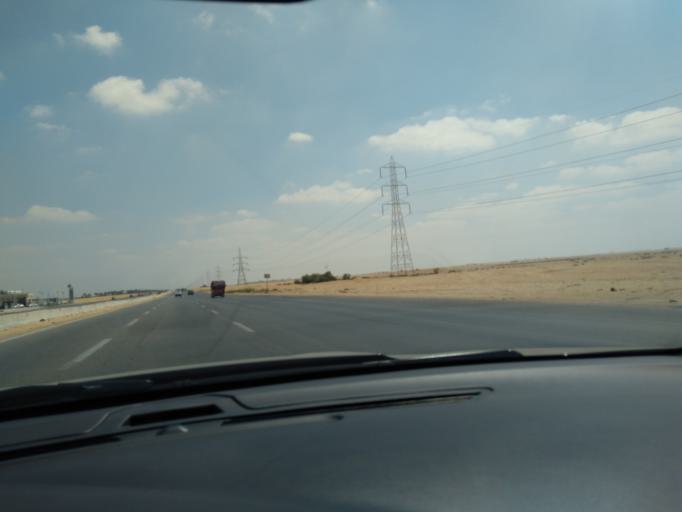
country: EG
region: Al Isma'iliyah
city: At Tall al Kabir
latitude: 30.3750
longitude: 31.9341
